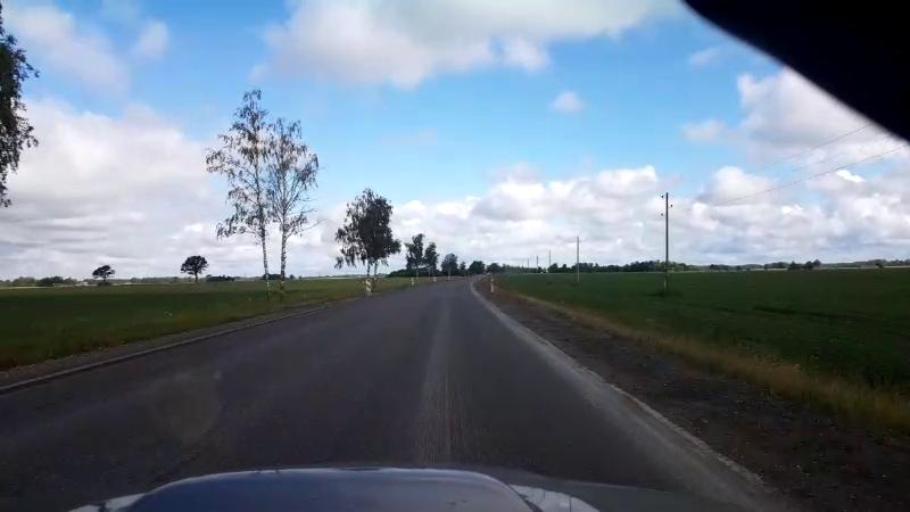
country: LV
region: Bauskas Rajons
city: Bauska
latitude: 56.3359
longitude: 24.2963
